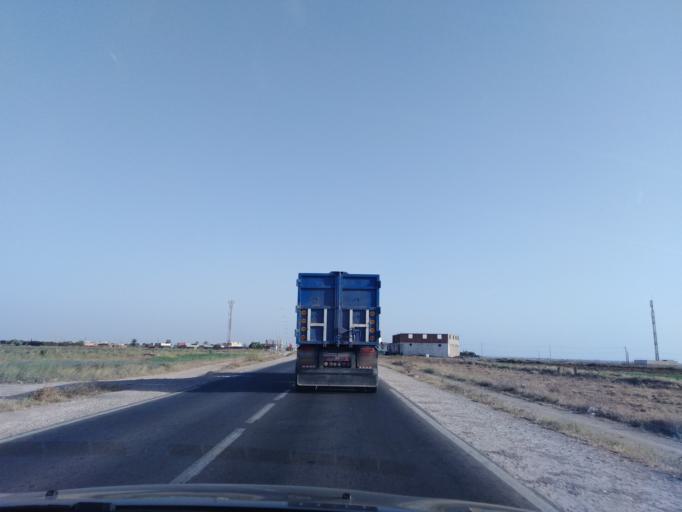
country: MA
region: Doukkala-Abda
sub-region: El-Jadida
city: Sidi Bennour
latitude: 32.5600
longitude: -8.7253
